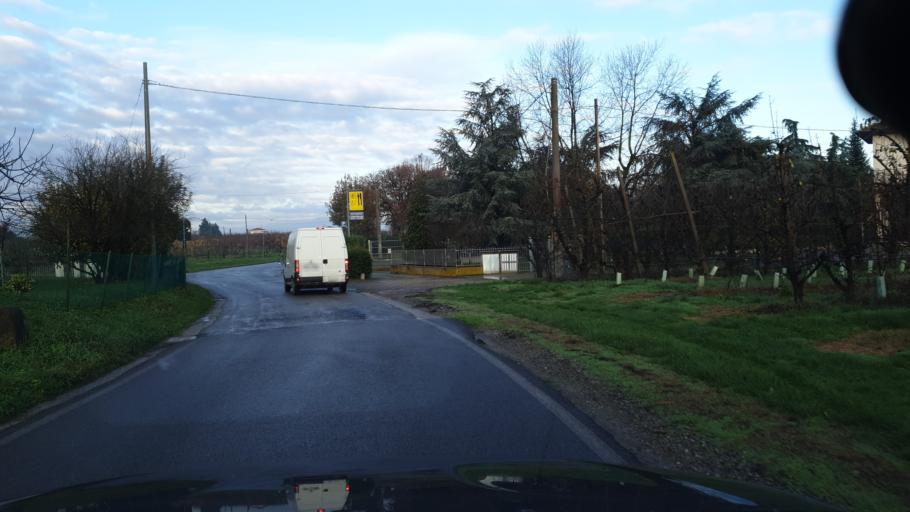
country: IT
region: Emilia-Romagna
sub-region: Provincia di Bologna
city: Crespellano
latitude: 44.5214
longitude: 11.1222
